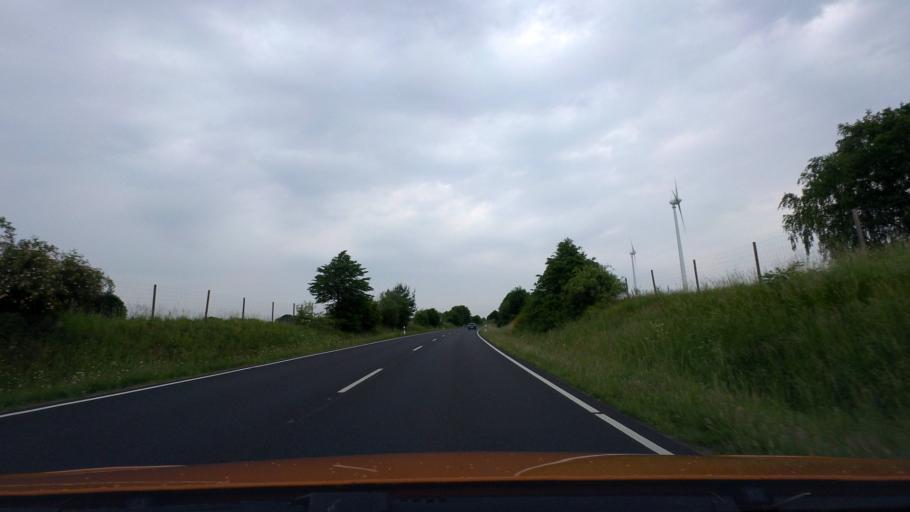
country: DE
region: Lower Saxony
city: Binnen
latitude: 52.6634
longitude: 9.1029
